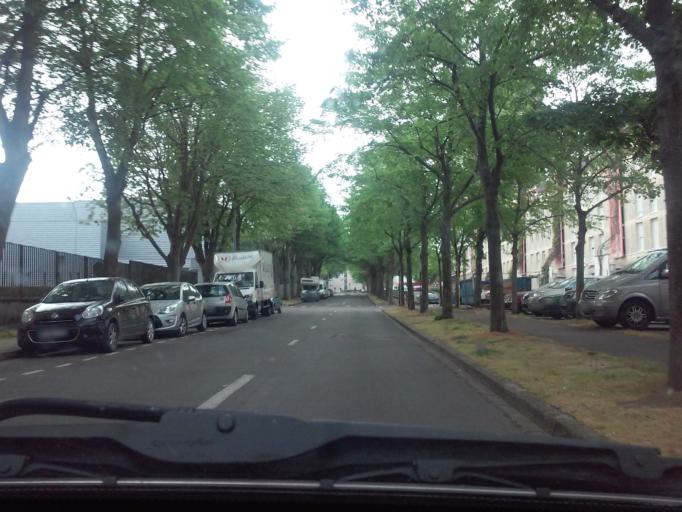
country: FR
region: Brittany
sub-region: Departement d'Ille-et-Vilaine
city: Rennes
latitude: 48.0928
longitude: -1.6803
